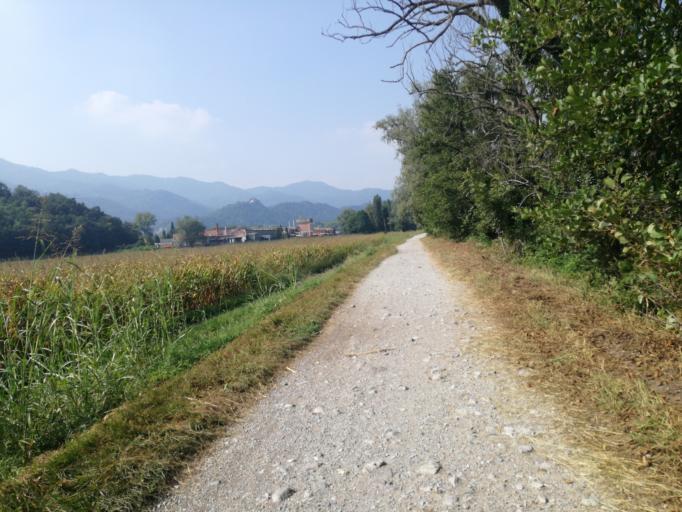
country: IT
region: Lombardy
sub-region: Provincia di Lecco
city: Brivio
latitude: 45.7515
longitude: 9.4491
